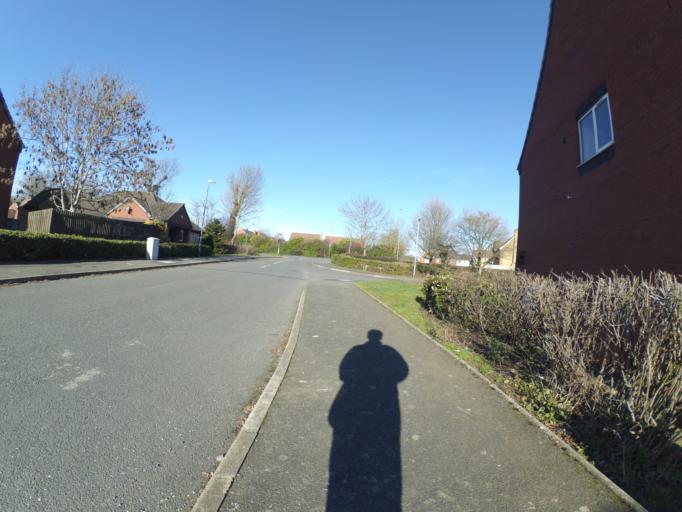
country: GB
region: England
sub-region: Warwickshire
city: Rugby
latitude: 52.3942
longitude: -1.2460
